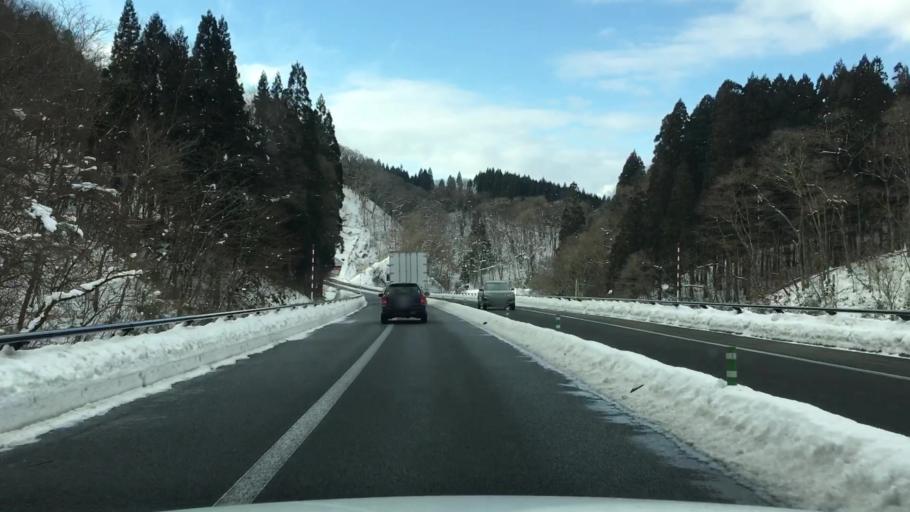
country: JP
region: Akita
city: Takanosu
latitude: 40.2249
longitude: 140.4346
